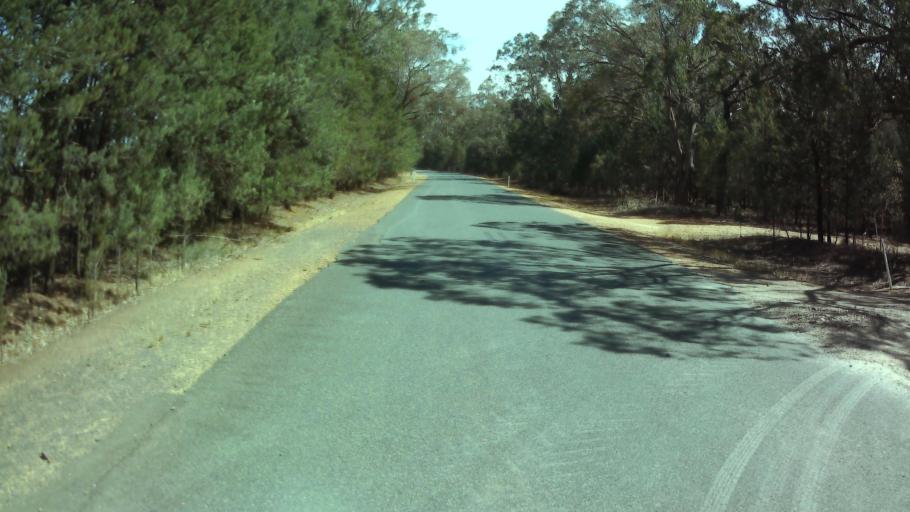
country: AU
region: New South Wales
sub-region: Weddin
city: Grenfell
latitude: -34.0119
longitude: 148.1294
